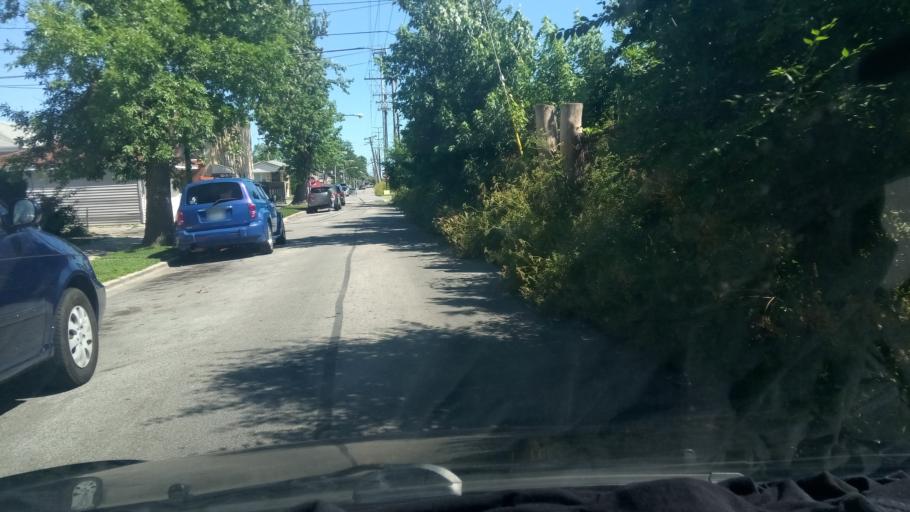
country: US
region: Illinois
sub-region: Cook County
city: Hometown
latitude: 41.7631
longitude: -87.7129
